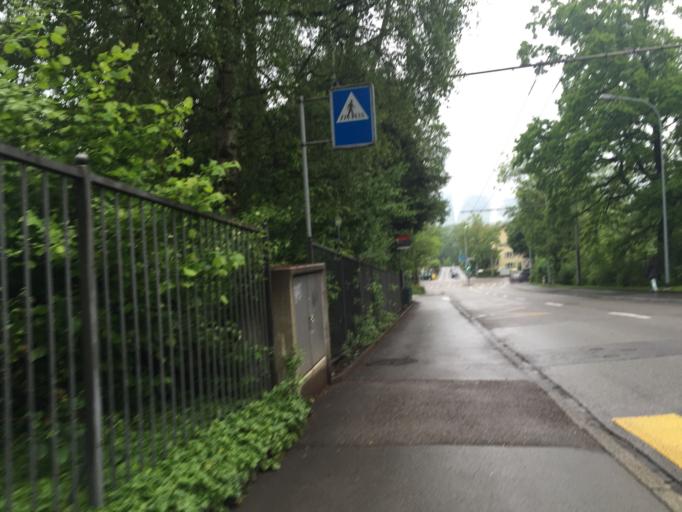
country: CH
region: Saint Gallen
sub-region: Wahlkreis St. Gallen
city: Sankt Gallen
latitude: 47.4095
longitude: 9.3368
